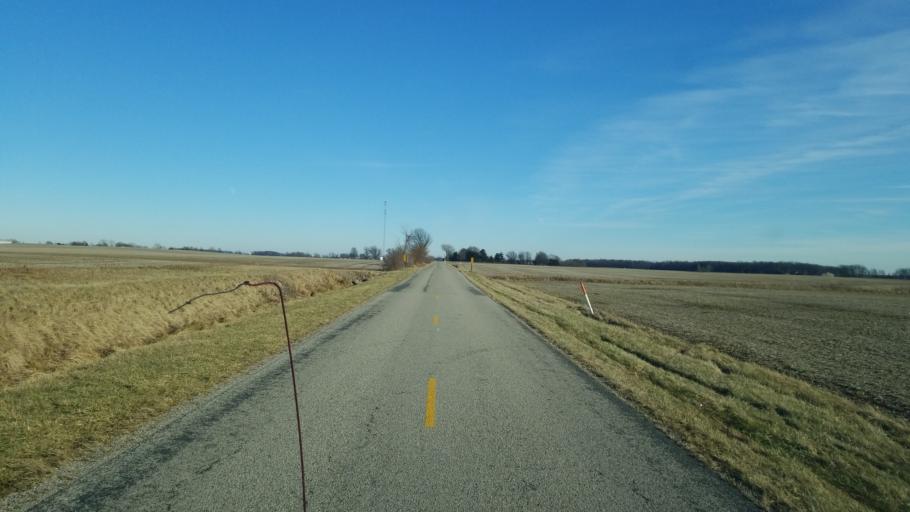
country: US
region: Ohio
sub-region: Sandusky County
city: Mount Carmel
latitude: 41.2561
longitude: -82.9668
